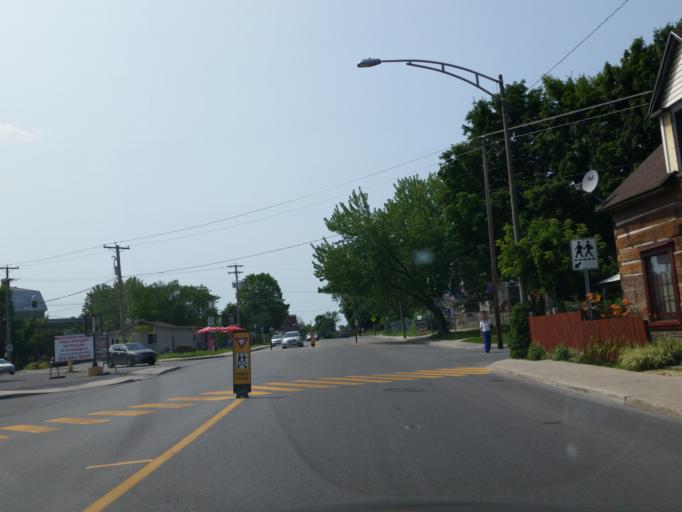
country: CA
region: Ontario
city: Bells Corners
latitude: 45.3968
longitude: -75.8466
